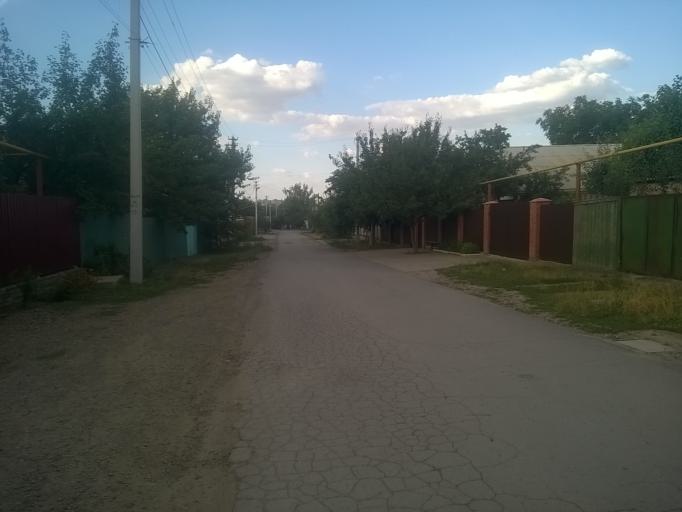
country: RU
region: Rostov
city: Donetsk
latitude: 48.3394
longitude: 39.9582
